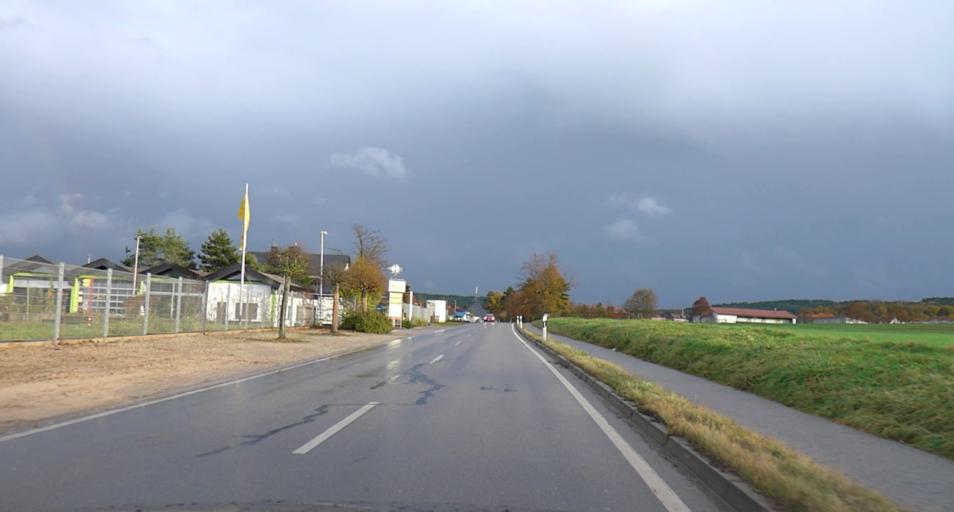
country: DE
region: Bavaria
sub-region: Upper Franconia
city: Langensendelbach
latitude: 49.6418
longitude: 11.0599
